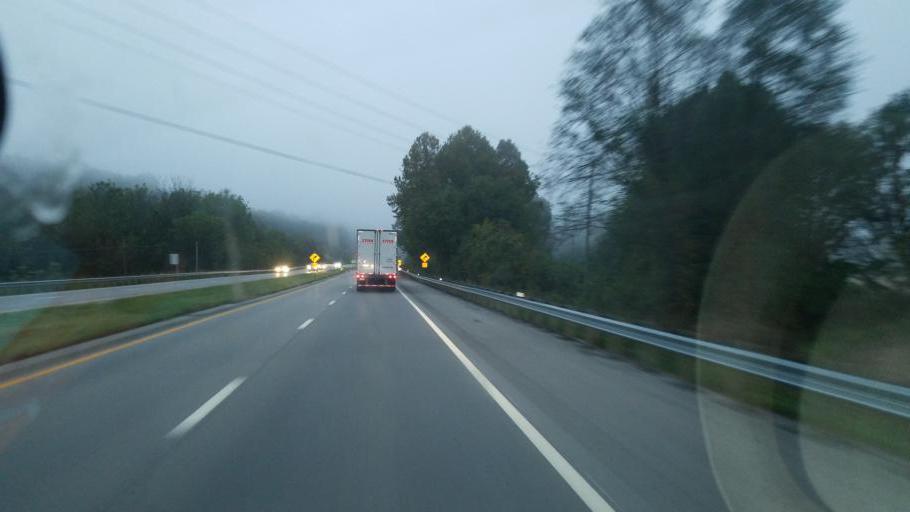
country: US
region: Ohio
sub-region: Pike County
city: Piketon
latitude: 39.0752
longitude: -83.0049
